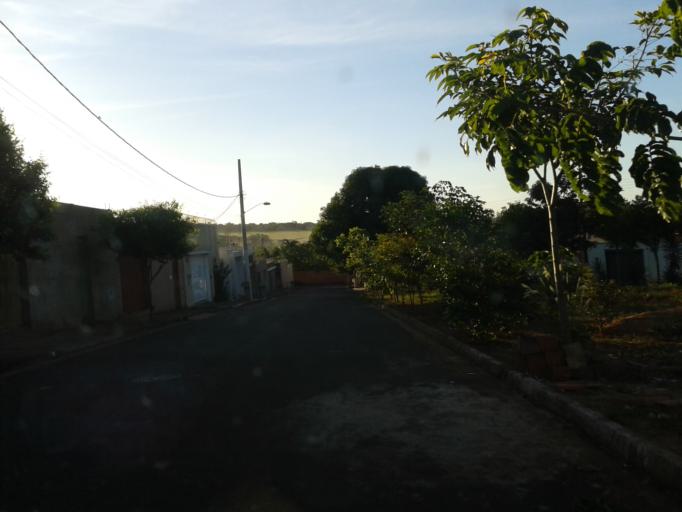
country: BR
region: Minas Gerais
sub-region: Ituiutaba
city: Ituiutaba
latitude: -18.9785
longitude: -49.4908
